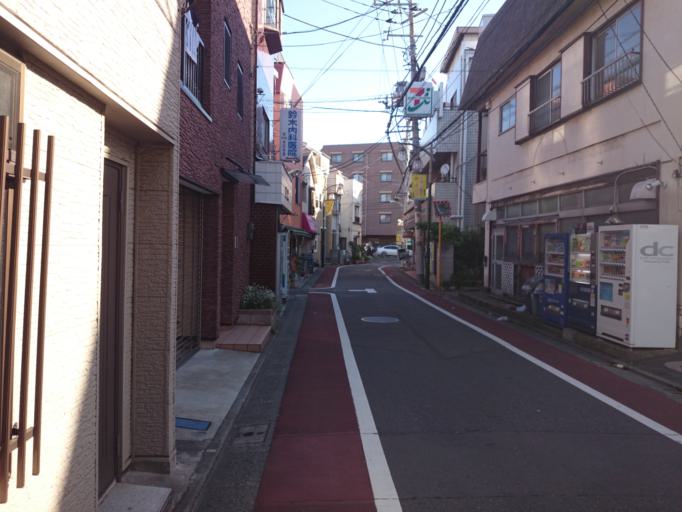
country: JP
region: Kanagawa
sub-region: Kawasaki-shi
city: Kawasaki
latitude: 35.6036
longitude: 139.7369
